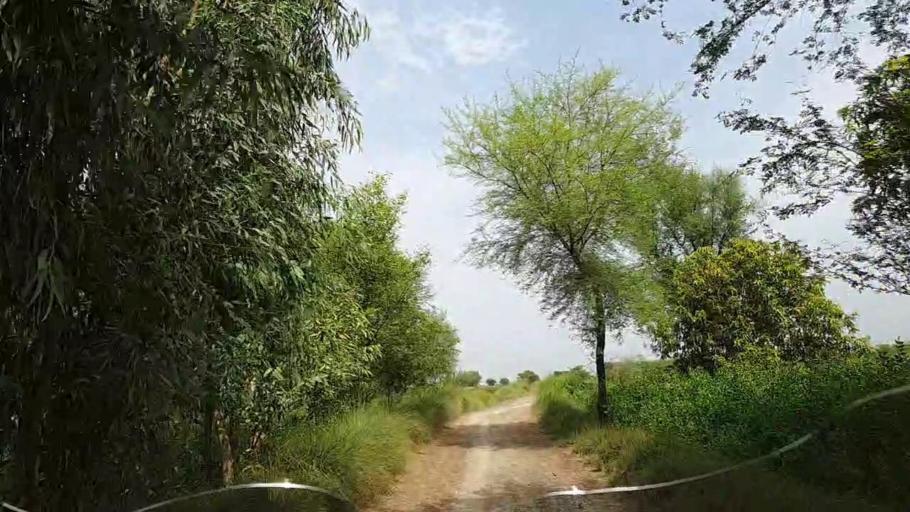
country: PK
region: Sindh
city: Naushahro Firoz
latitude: 26.8894
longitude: 68.0755
